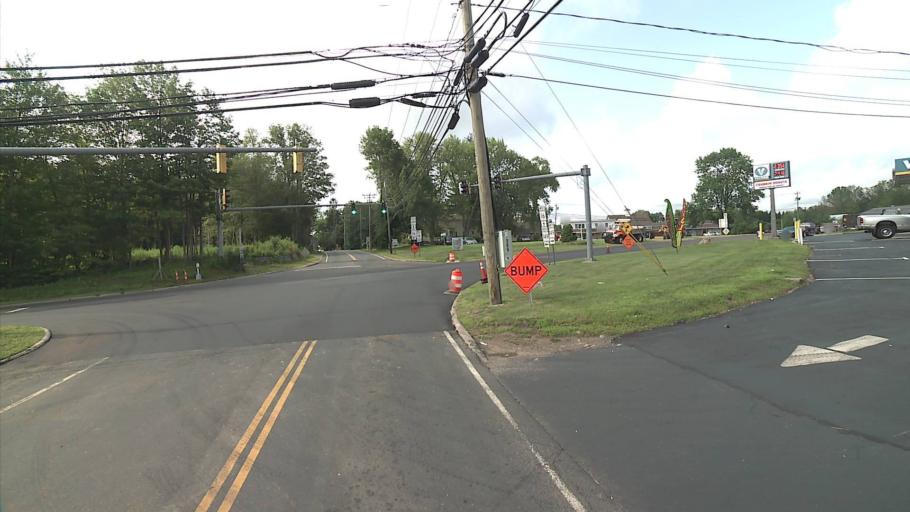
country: US
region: Connecticut
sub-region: Middlesex County
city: Moodus
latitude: 41.5458
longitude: -72.4131
